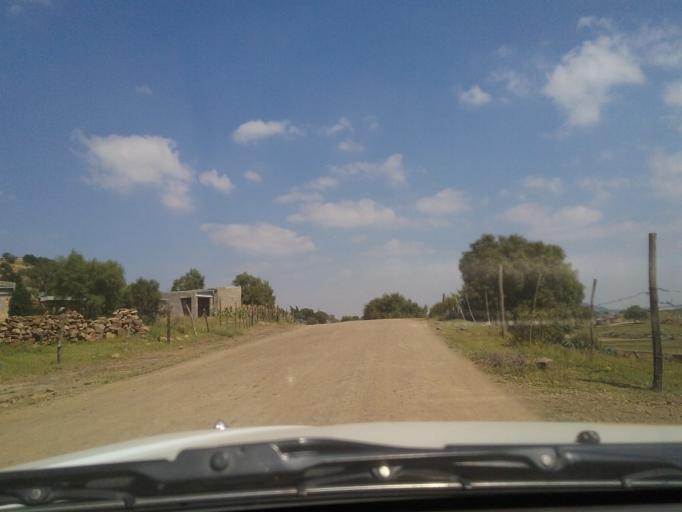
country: LS
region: Maseru
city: Maseru
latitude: -29.4012
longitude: 27.4398
